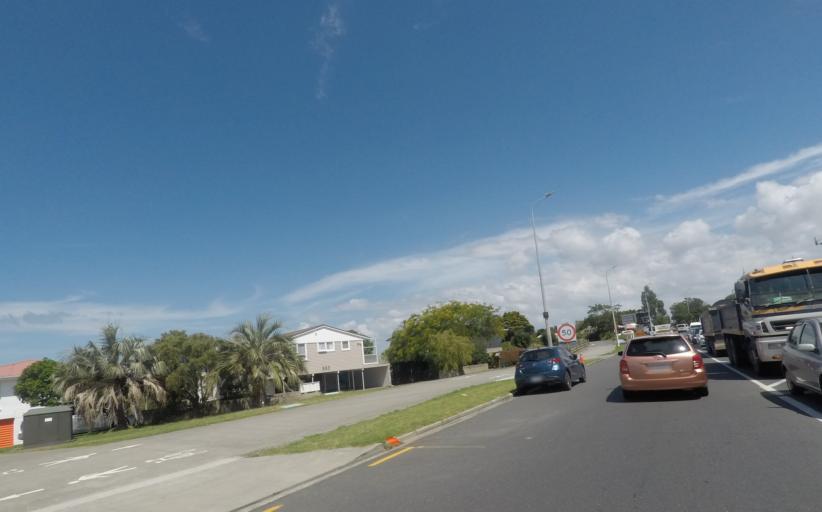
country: NZ
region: Auckland
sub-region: Auckland
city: Tamaki
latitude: -36.8688
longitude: 174.8455
